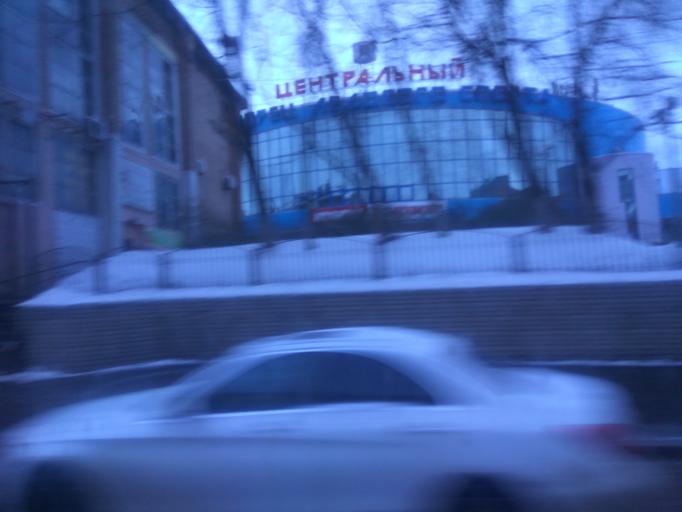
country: RU
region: Moscow
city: Taganskiy
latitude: 55.7306
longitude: 37.6800
